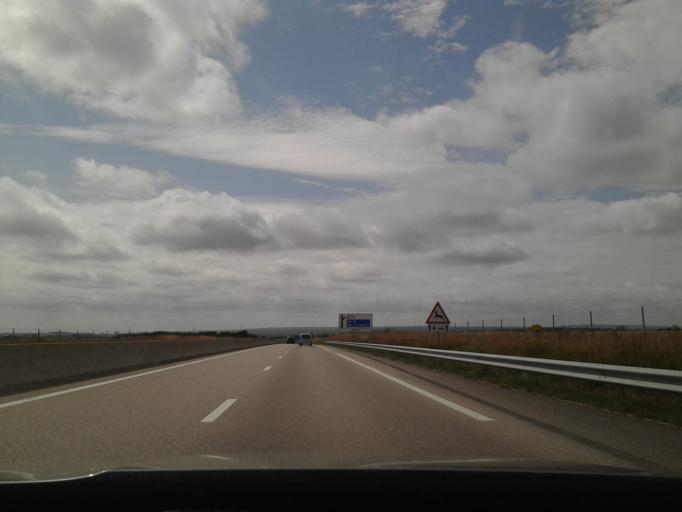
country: FR
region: Lower Normandy
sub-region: Departement de l'Orne
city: Ecouche
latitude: 48.7415
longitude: -0.0747
